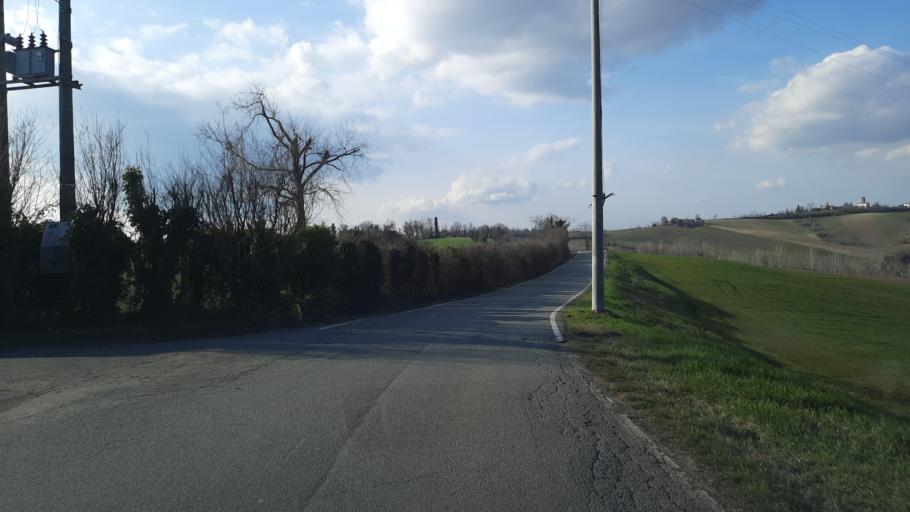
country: IT
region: Piedmont
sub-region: Provincia di Alessandria
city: San Giorgio
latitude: 45.1161
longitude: 8.3935
